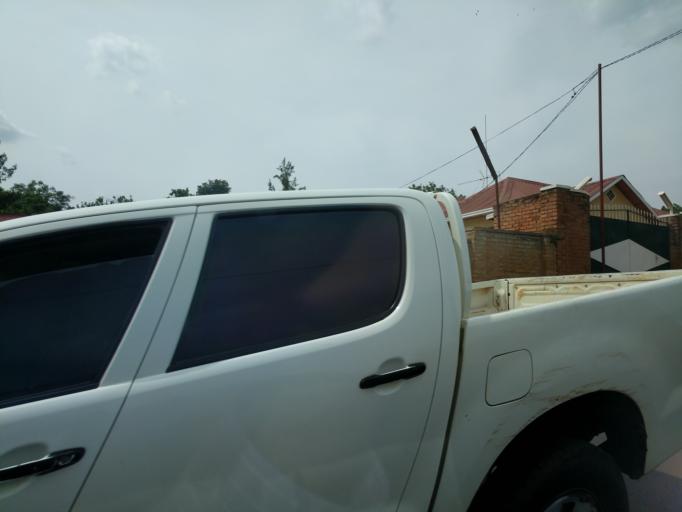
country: RW
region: Kigali
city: Kigali
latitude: -1.9726
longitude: 30.1222
